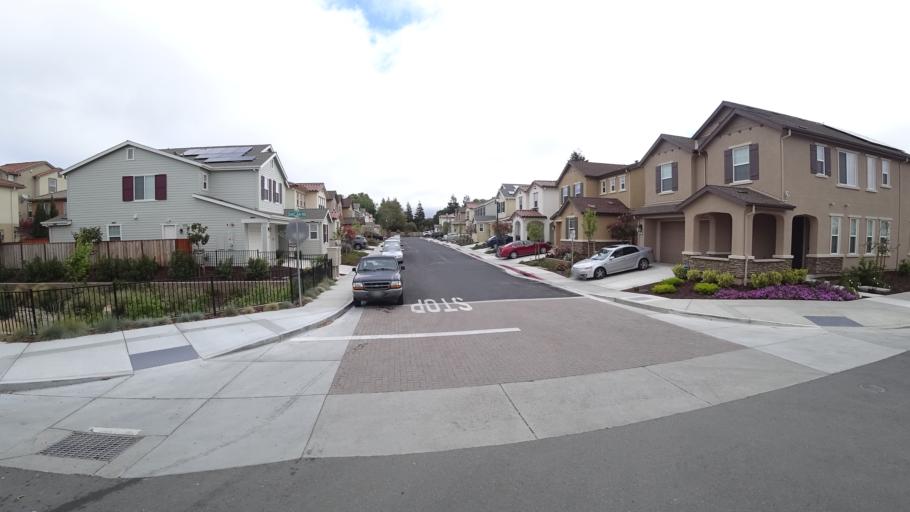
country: US
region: California
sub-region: Alameda County
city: San Lorenzo
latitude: 37.6453
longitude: -122.1185
